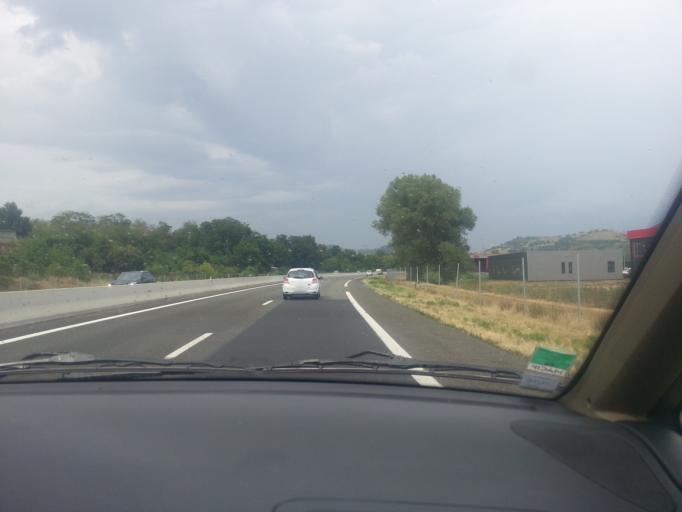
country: FR
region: Auvergne
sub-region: Departement du Puy-de-Dome
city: Issoire
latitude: 45.5348
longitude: 3.2589
